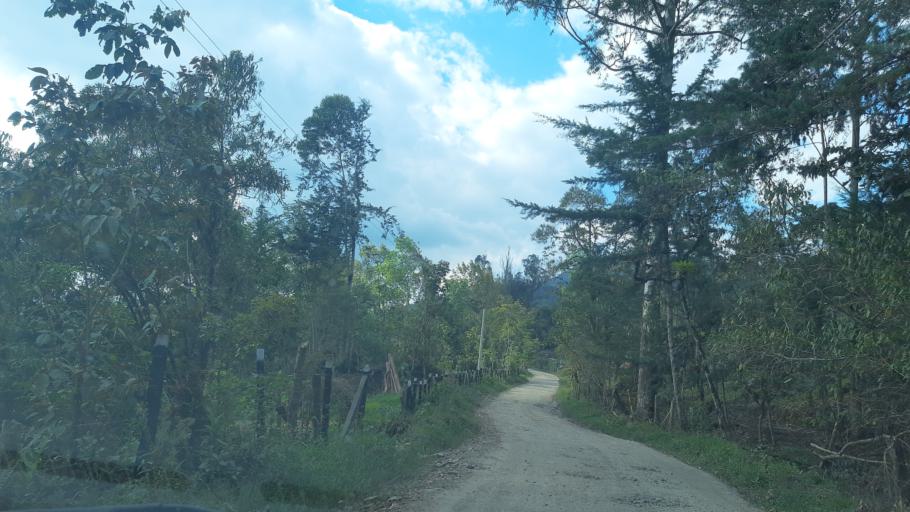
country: CO
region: Boyaca
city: Garagoa
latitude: 5.0877
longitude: -73.3358
